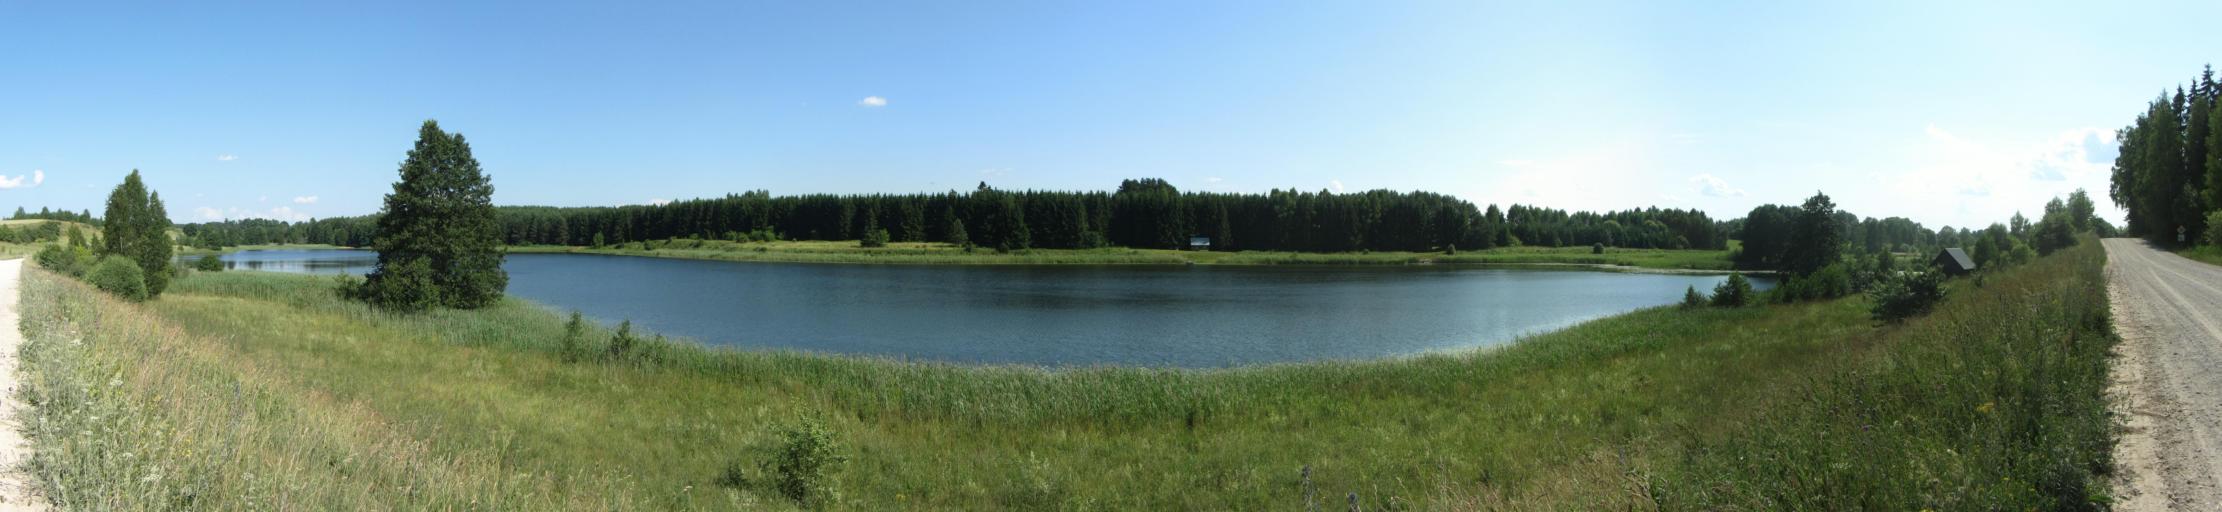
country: LT
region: Utenos apskritis
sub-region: Anyksciai
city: Anyksciai
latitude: 55.3192
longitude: 25.1118
